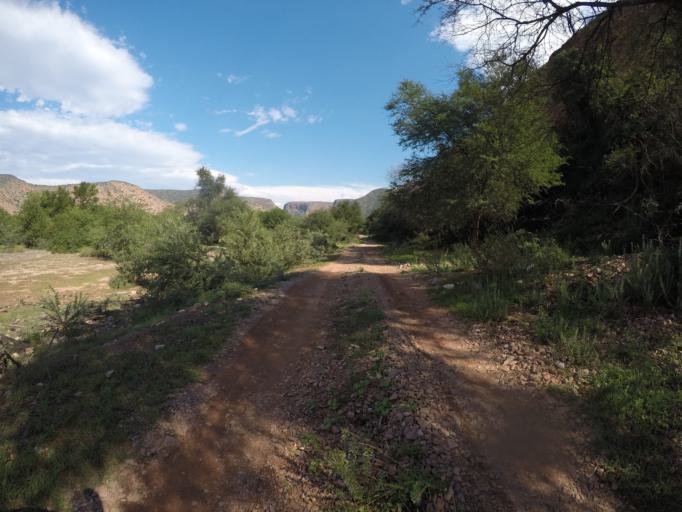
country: ZA
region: Eastern Cape
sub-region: Cacadu District Municipality
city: Kareedouw
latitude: -33.6626
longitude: 24.3920
